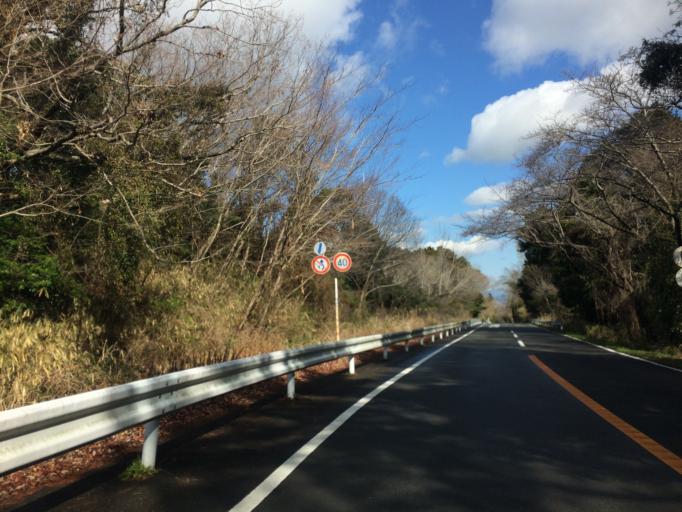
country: JP
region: Shizuoka
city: Shizuoka-shi
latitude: 34.9672
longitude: 138.4479
